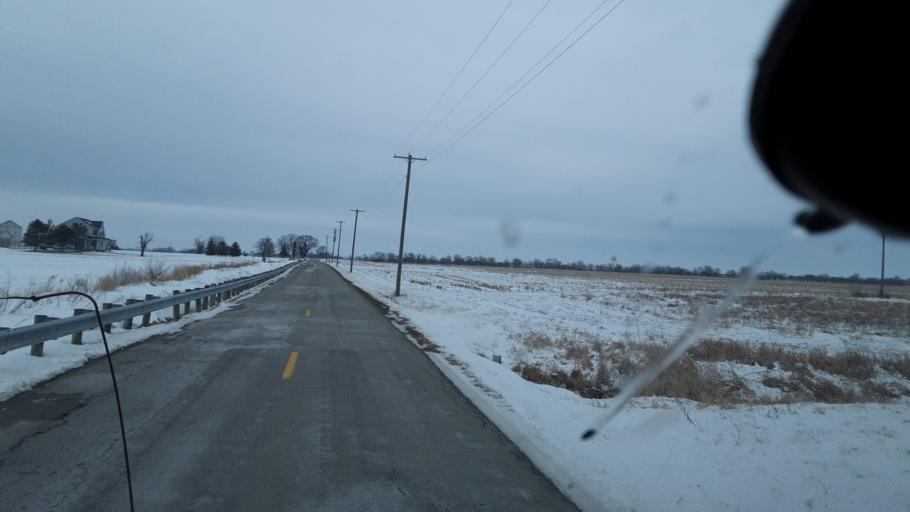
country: US
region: Ohio
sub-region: Madison County
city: Mount Sterling
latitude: 39.7188
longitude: -83.2988
